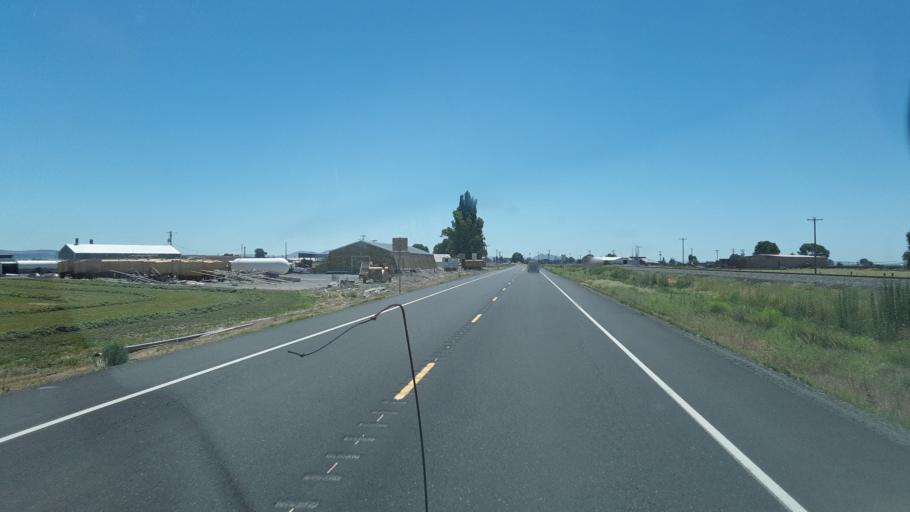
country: US
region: California
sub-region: Siskiyou County
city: Tulelake
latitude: 42.0029
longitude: -121.5247
